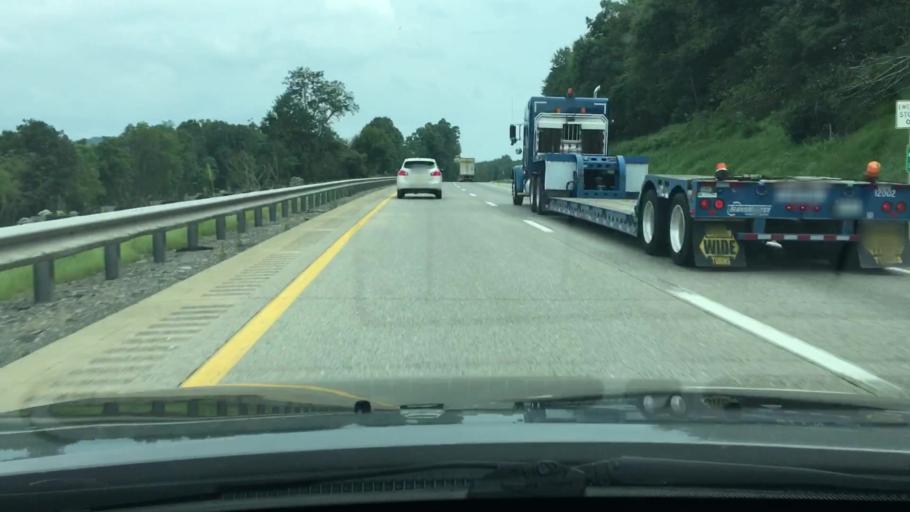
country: US
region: Pennsylvania
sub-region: Lebanon County
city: Jonestown
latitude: 40.4766
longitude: -76.5252
